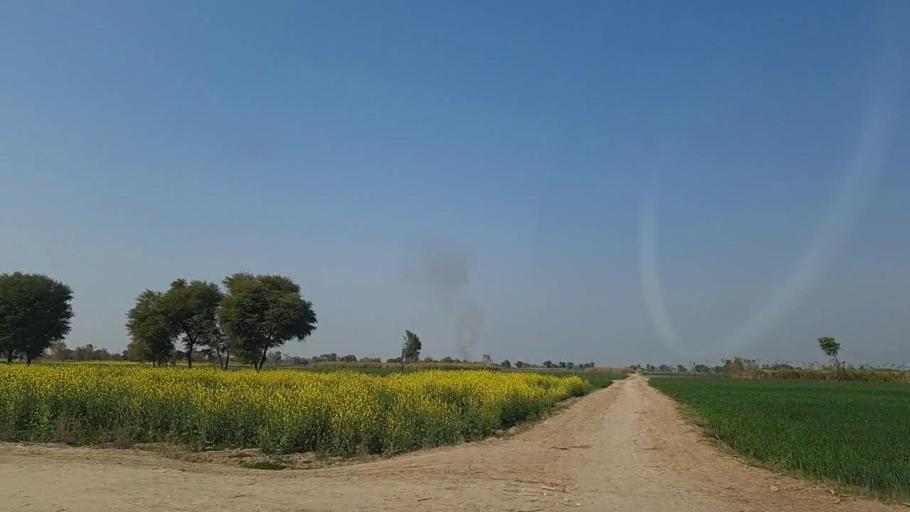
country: PK
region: Sindh
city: Daur
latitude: 26.4413
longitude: 68.2628
